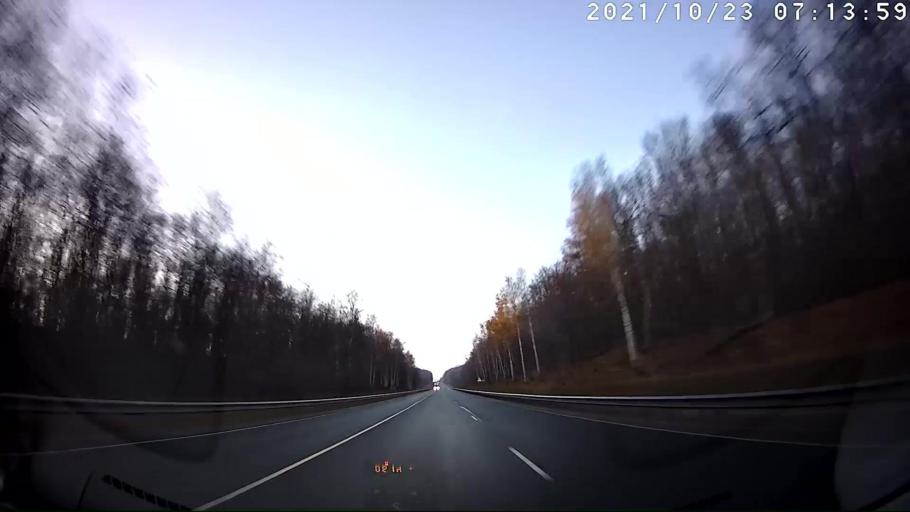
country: RU
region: Saratov
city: Khvalynsk
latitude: 52.5114
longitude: 48.0164
